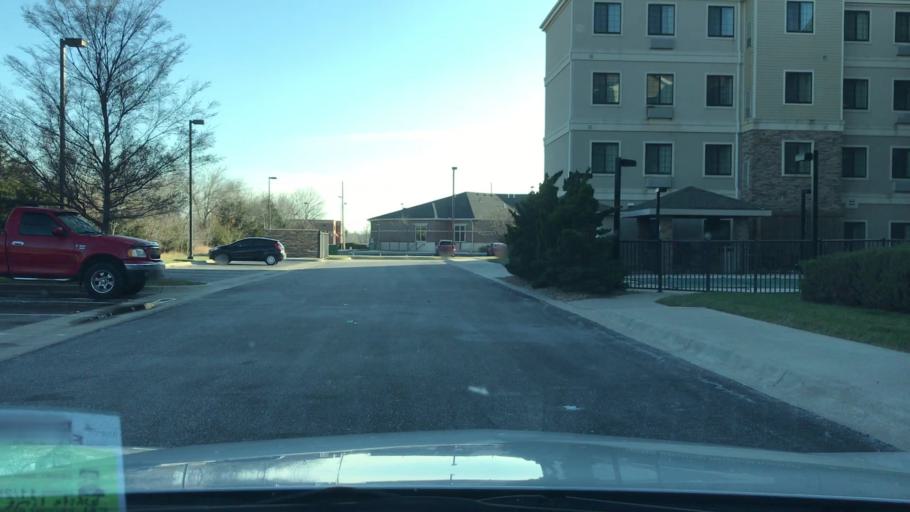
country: US
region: Kansas
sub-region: Butler County
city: Andover
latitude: 37.7246
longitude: -97.2054
